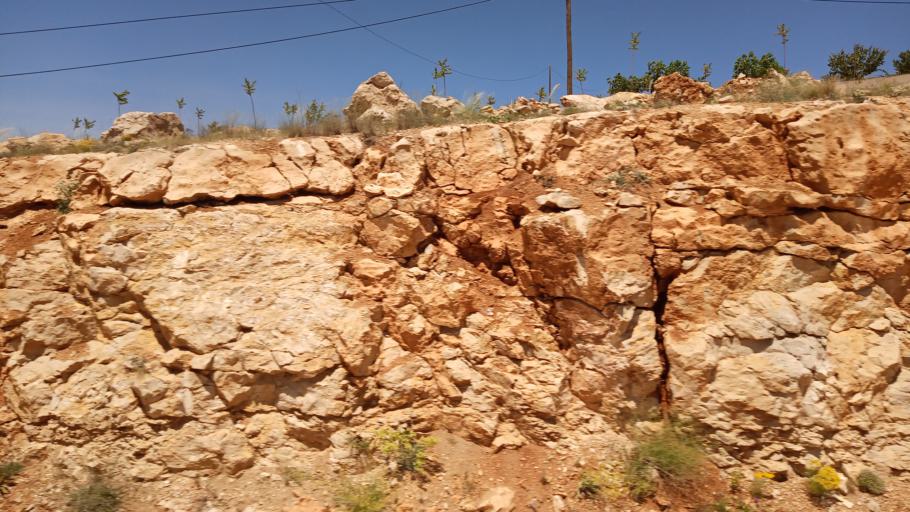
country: TR
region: Malatya
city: Darende
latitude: 38.6228
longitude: 37.4506
